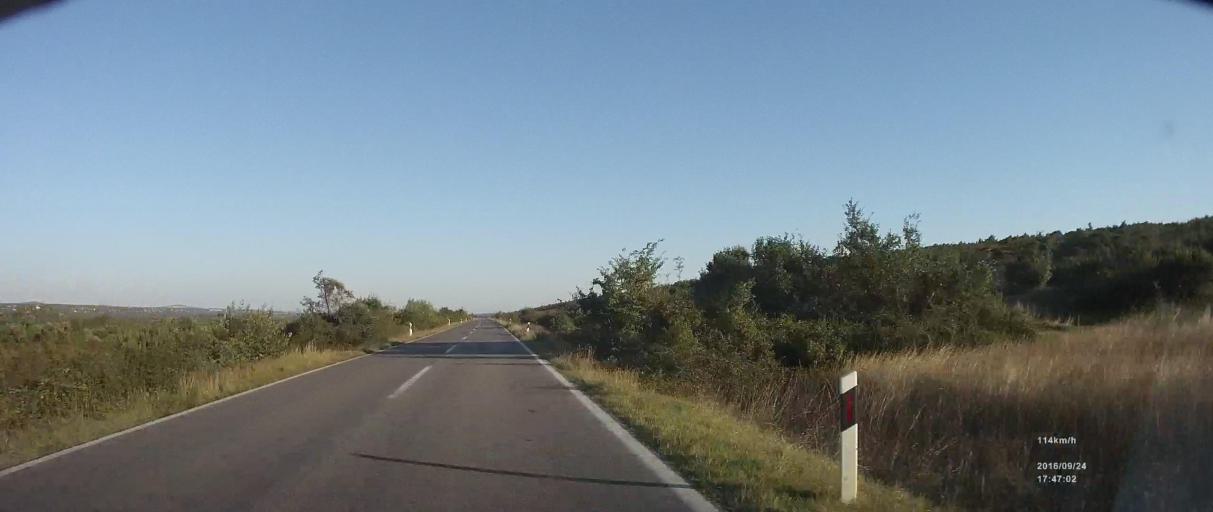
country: HR
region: Zadarska
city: Polaca
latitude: 44.0803
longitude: 15.5166
